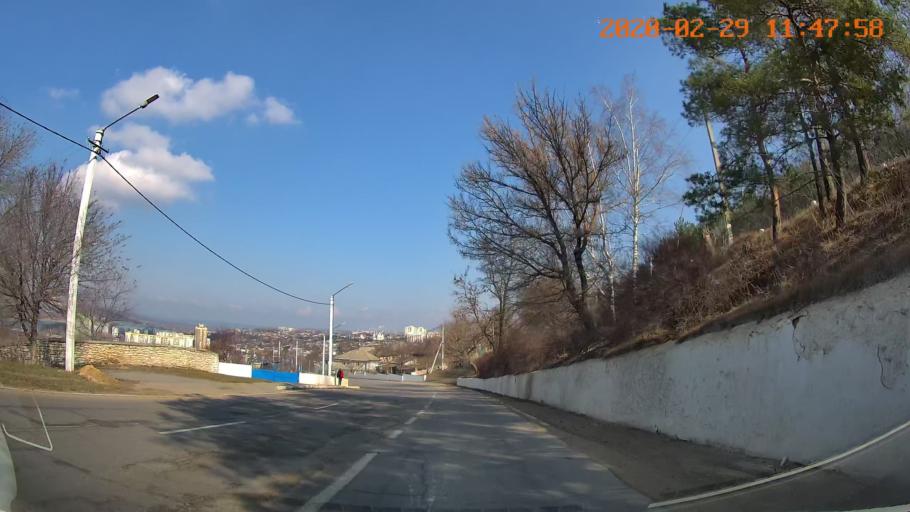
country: MD
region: Rezina
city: Rezina
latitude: 47.7450
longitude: 28.9885
